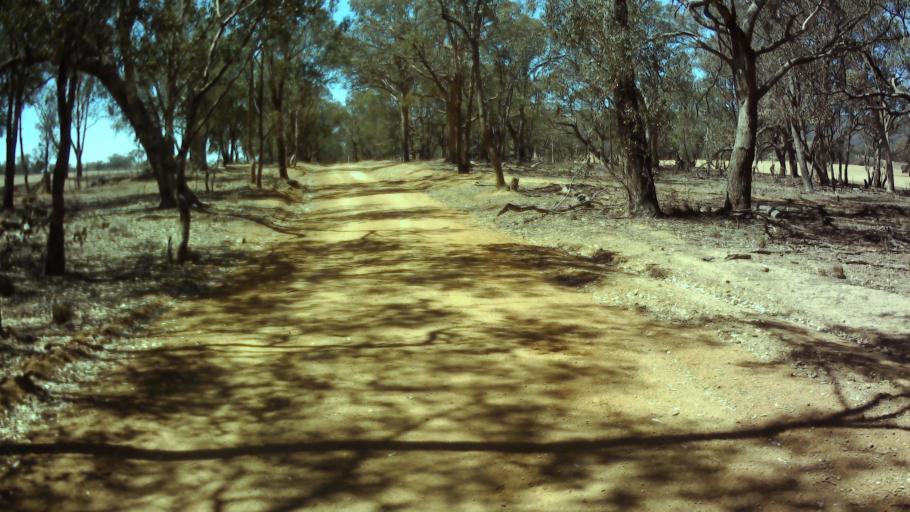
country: AU
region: New South Wales
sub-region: Weddin
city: Grenfell
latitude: -33.9569
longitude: 148.0849
